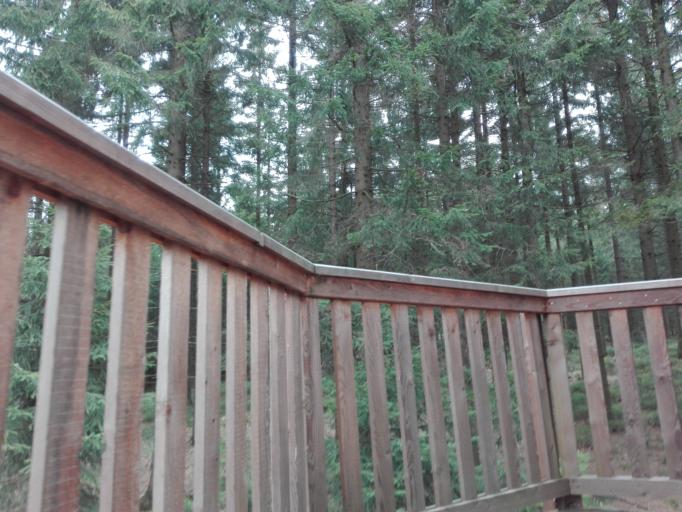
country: AT
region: Upper Austria
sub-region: Politischer Bezirk Rohrbach
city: Ulrichsberg
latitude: 48.7041
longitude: 13.9531
